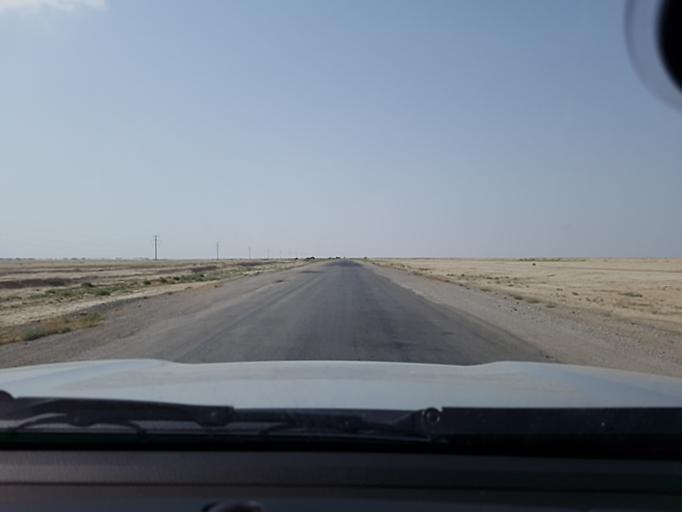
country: TM
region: Balkan
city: Gumdag
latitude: 38.8898
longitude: 54.5929
